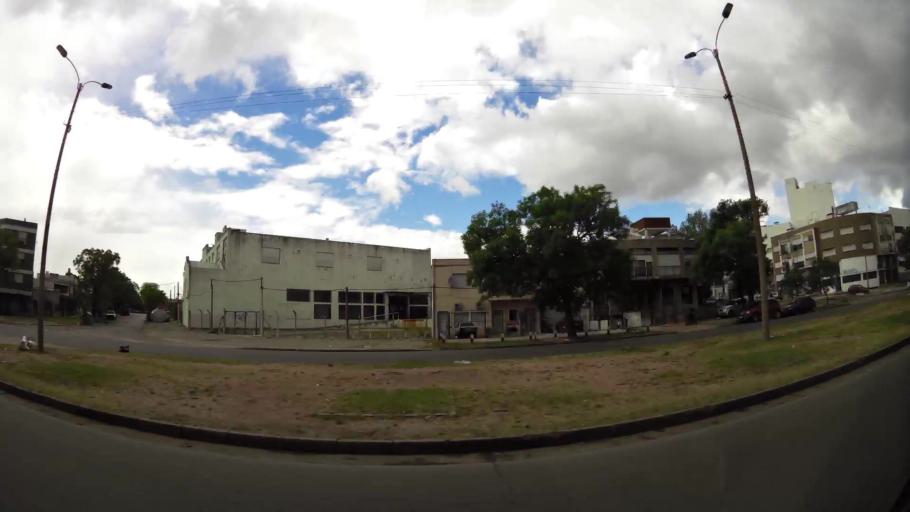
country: UY
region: Montevideo
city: Montevideo
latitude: -34.8728
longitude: -56.1525
